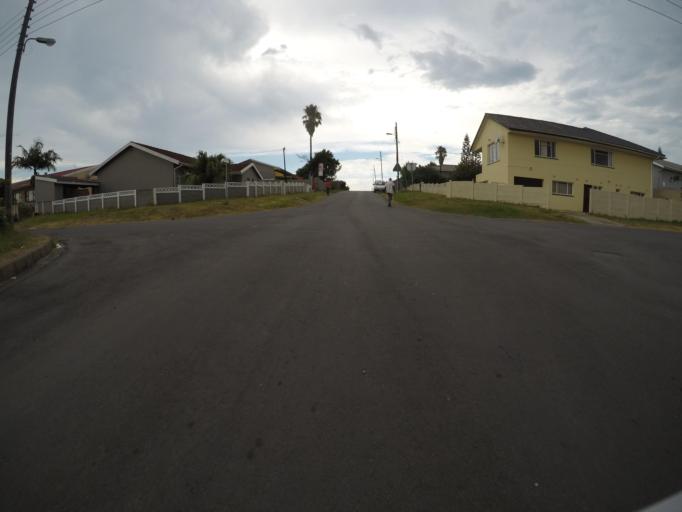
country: ZA
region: Eastern Cape
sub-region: Buffalo City Metropolitan Municipality
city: East London
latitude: -33.0231
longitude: 27.8654
